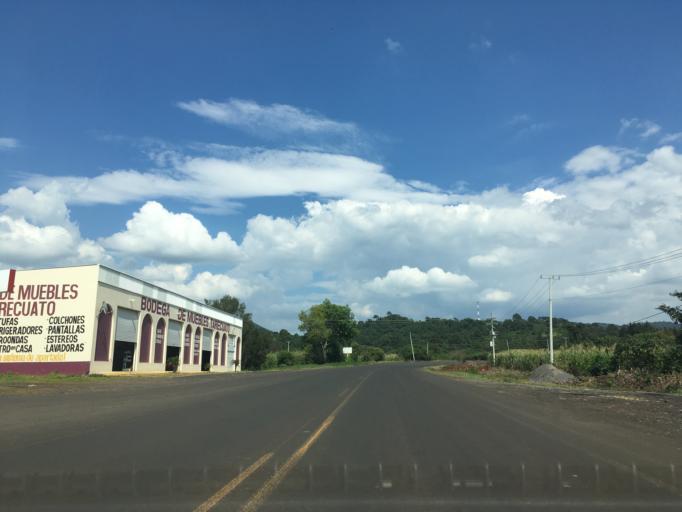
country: MX
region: Michoacan
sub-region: Tingueindin
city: Tingueindin
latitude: 19.8436
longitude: -102.4798
